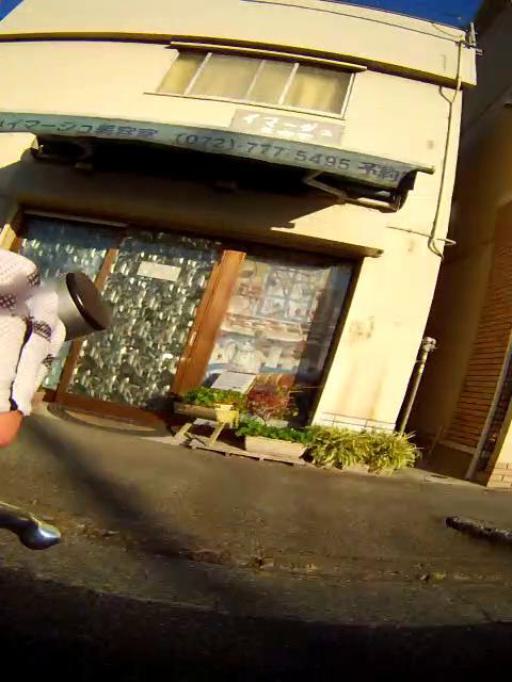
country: JP
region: Hyogo
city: Itami
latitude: 34.7629
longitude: 135.4116
